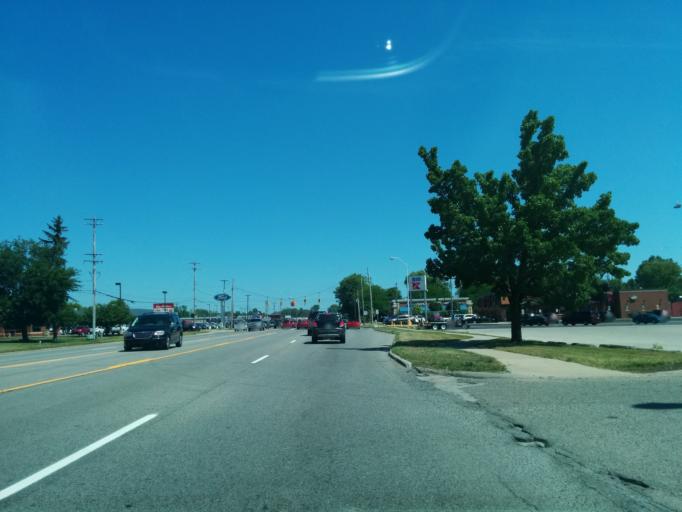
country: US
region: Michigan
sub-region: Bay County
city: Bay City
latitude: 43.6224
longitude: -83.9142
